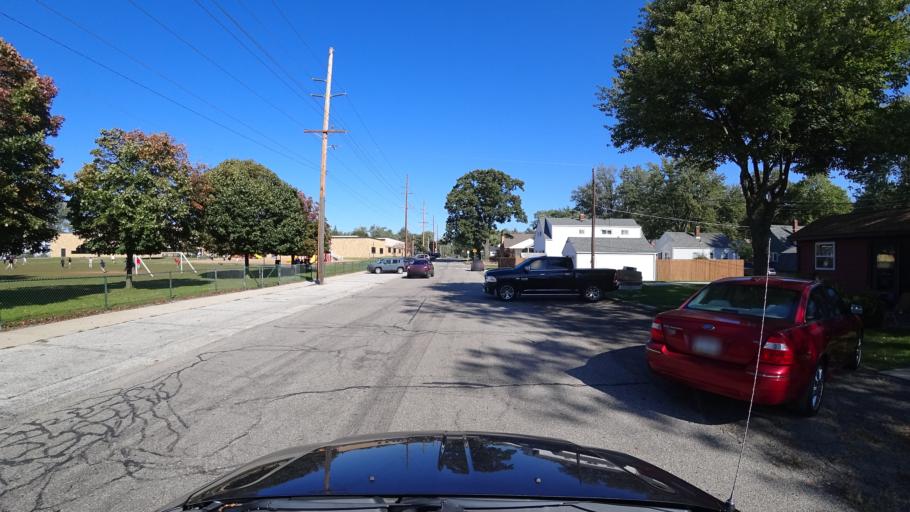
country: US
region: Indiana
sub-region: LaPorte County
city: Michigan City
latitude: 41.7061
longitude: -86.8907
